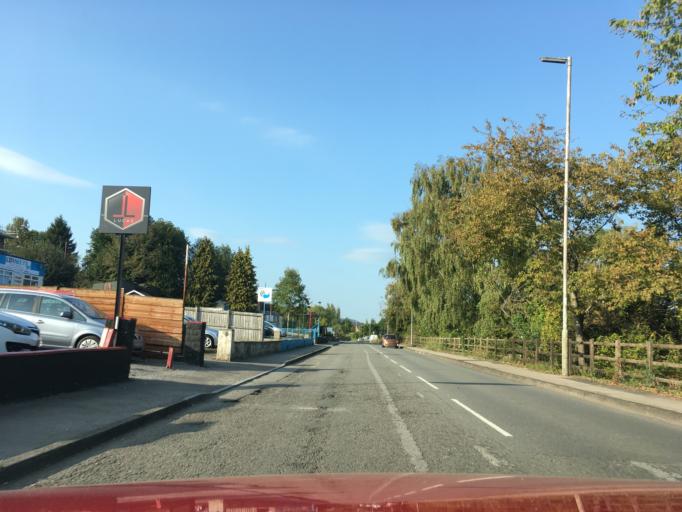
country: GB
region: Wales
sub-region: Torfaen County Borough
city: New Inn
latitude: 51.6782
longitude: -3.0206
